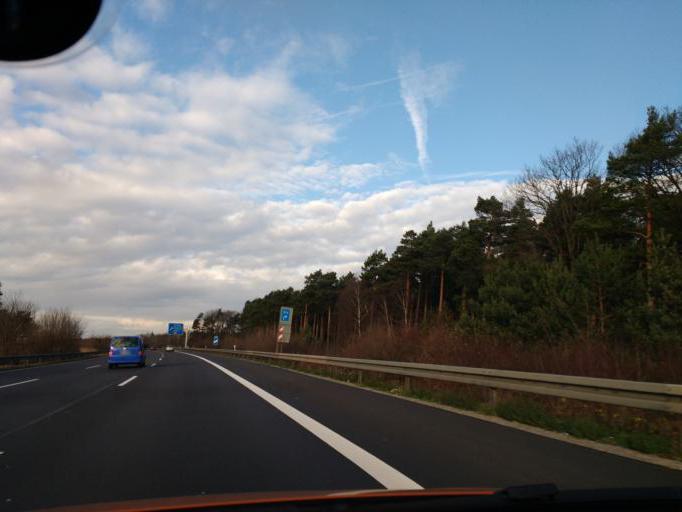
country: DE
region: Lower Saxony
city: Mariental
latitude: 52.2613
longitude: 10.9888
